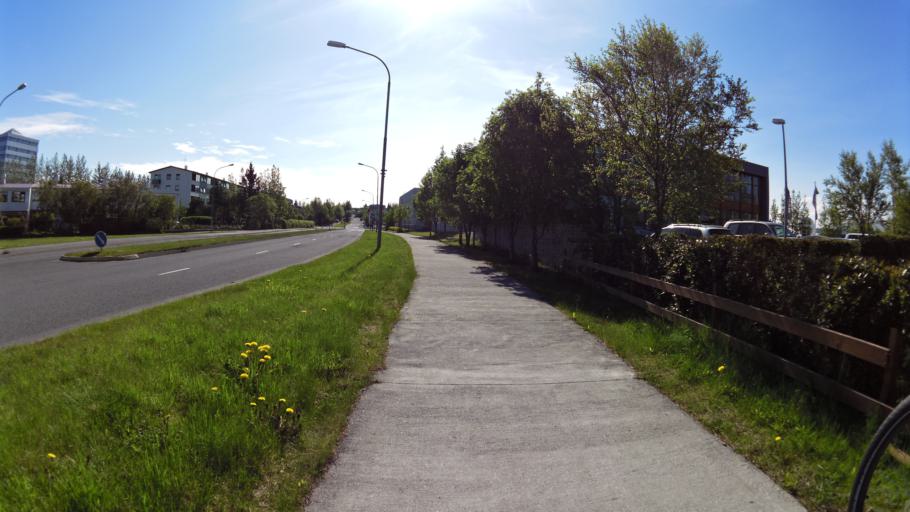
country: IS
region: Capital Region
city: Reykjavik
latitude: 64.1271
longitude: -21.8909
